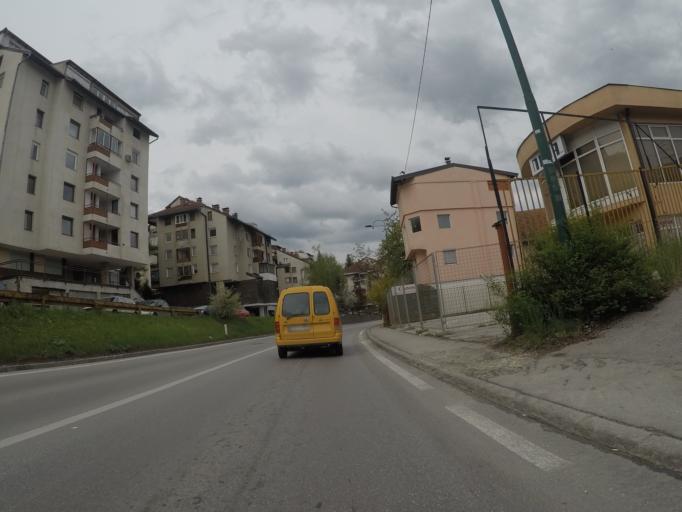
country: BA
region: Federation of Bosnia and Herzegovina
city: Kobilja Glava
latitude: 43.8477
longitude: 18.4006
